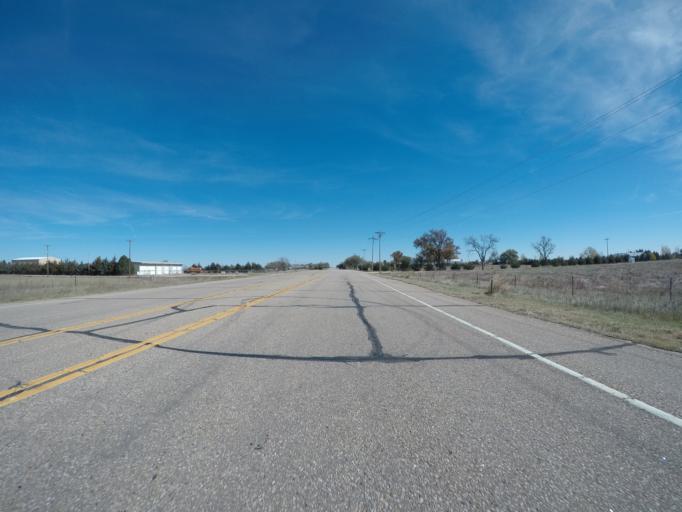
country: US
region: Colorado
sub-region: Yuma County
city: Yuma
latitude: 39.6559
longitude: -102.6892
